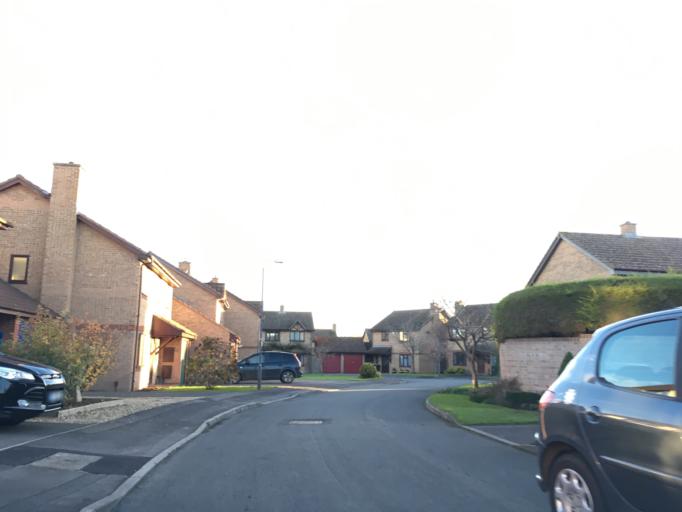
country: GB
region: England
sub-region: South Gloucestershire
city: Thornbury
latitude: 51.6134
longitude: -2.5100
